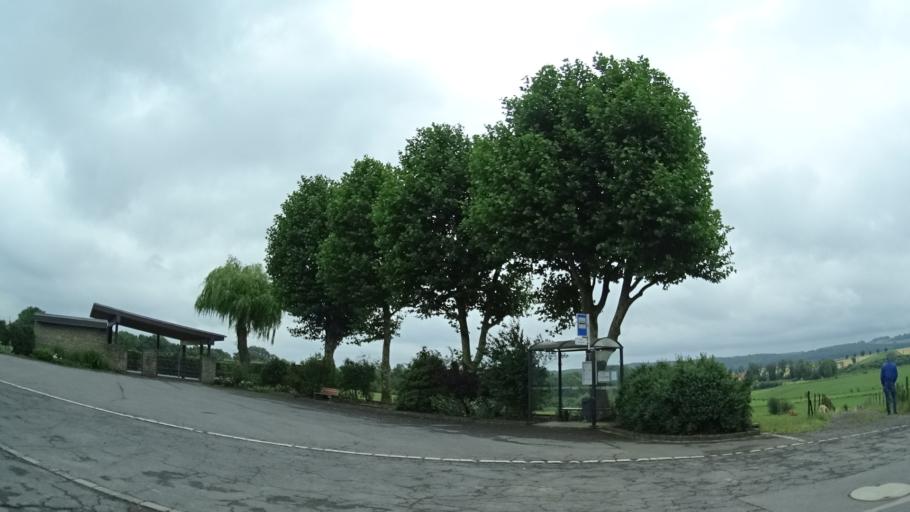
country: LU
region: Luxembourg
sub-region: Canton de Capellen
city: Steinfort
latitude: 49.6478
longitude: 5.9227
